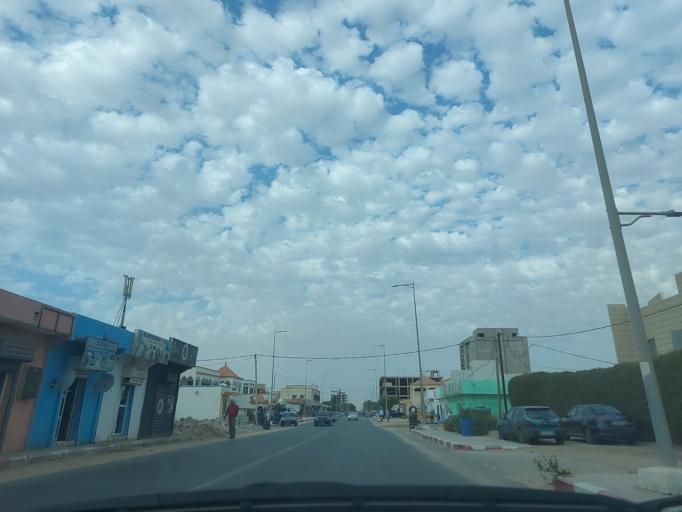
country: MR
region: Nouakchott
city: Nouakchott
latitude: 18.1104
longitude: -15.9923
